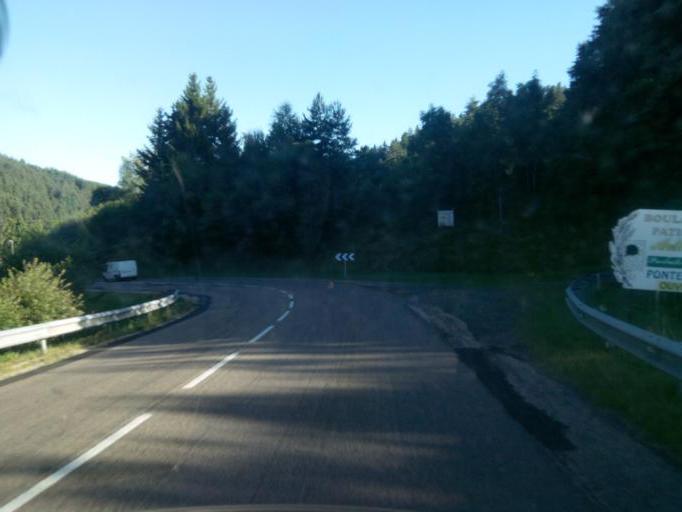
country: FR
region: Auvergne
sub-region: Departement de la Haute-Loire
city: Craponne-sur-Arzon
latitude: 45.3472
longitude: 3.8979
